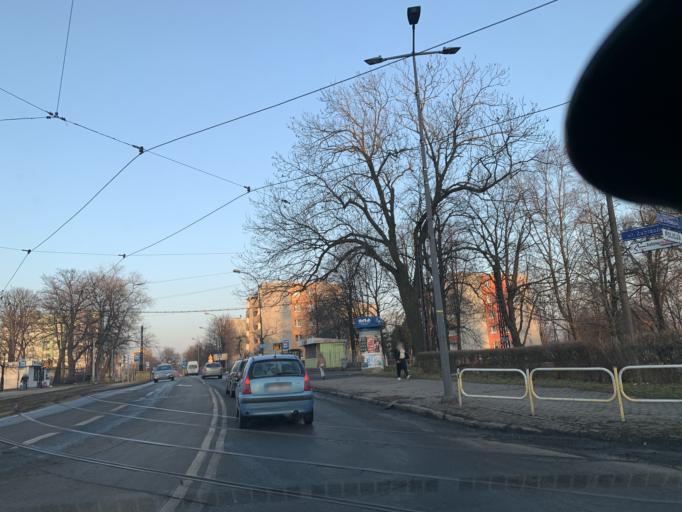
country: PL
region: Silesian Voivodeship
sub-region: Bytom
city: Bytom
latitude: 50.3363
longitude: 18.8969
